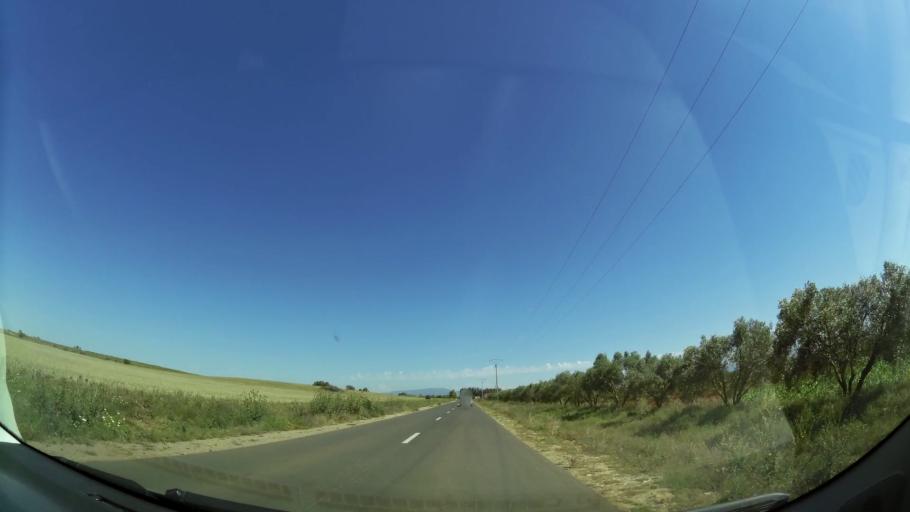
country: MA
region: Oriental
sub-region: Berkane-Taourirt
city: Madagh
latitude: 35.0308
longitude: -2.4141
